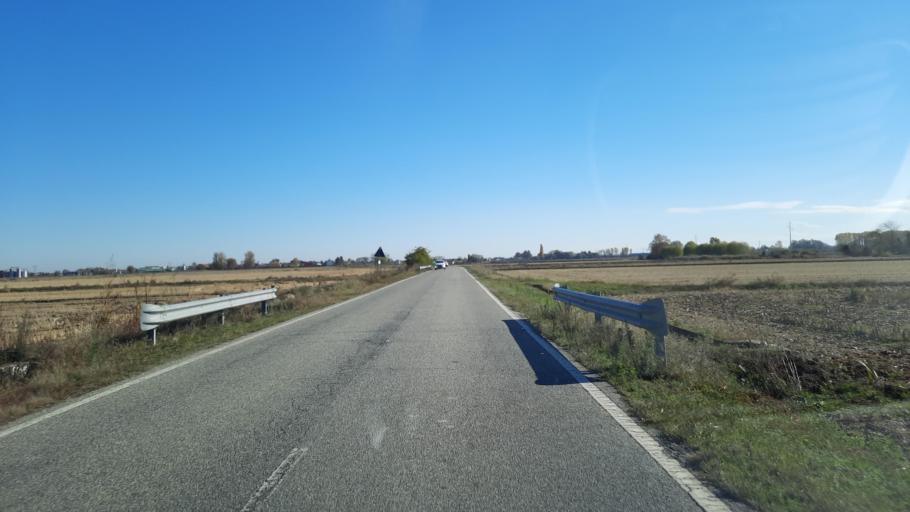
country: IT
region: Piedmont
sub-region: Provincia di Alessandria
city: Villanova Monferrato
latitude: 45.1805
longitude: 8.4535
